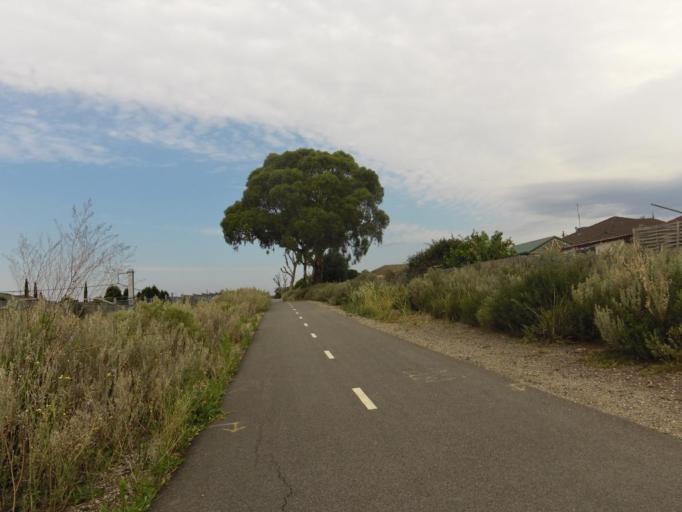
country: AU
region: Victoria
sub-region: Whittlesea
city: Epping
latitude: -37.6510
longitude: 145.0532
